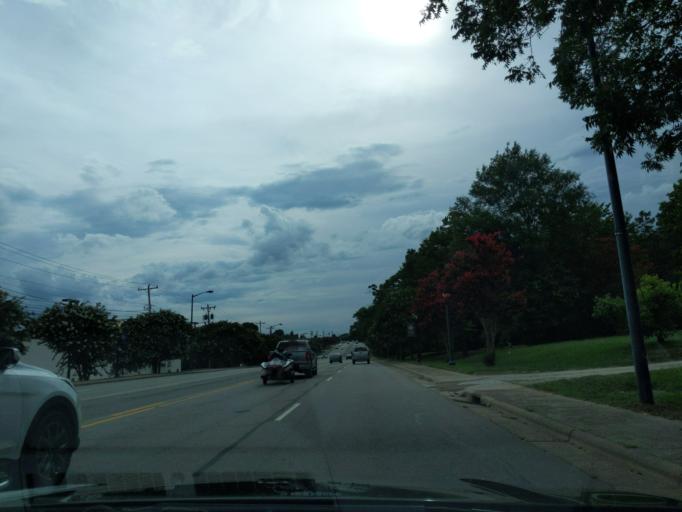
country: US
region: North Carolina
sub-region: Cabarrus County
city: Harrisburg
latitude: 35.3210
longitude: -80.6632
